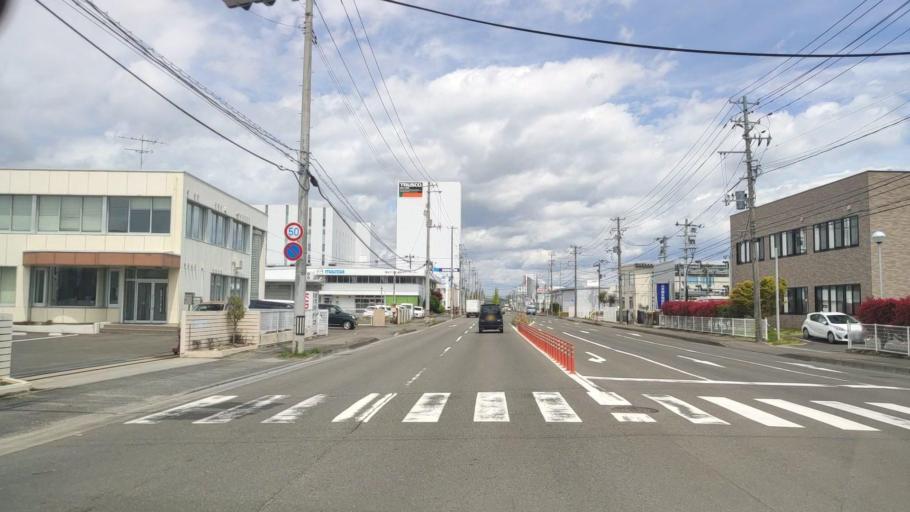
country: JP
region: Miyagi
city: Sendai-shi
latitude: 38.2656
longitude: 140.9434
